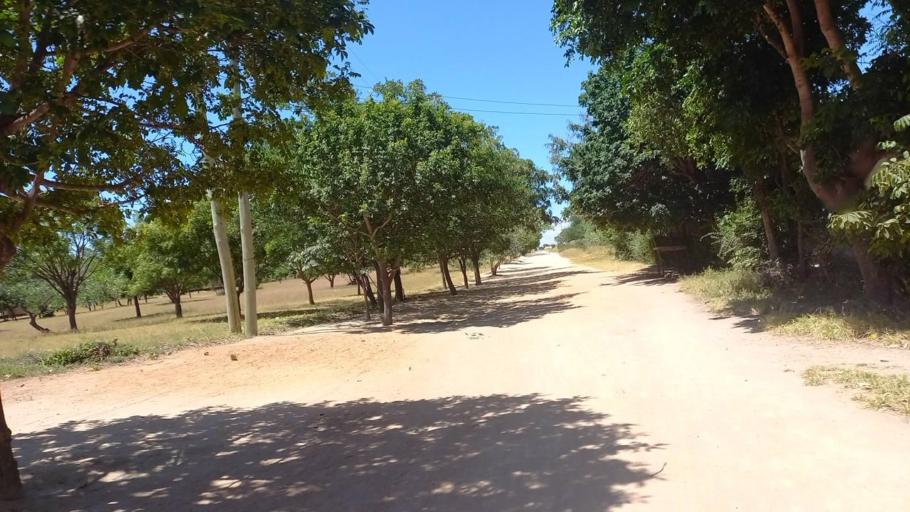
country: TZ
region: Dodoma
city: Dodoma
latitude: -6.1173
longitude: 35.7417
